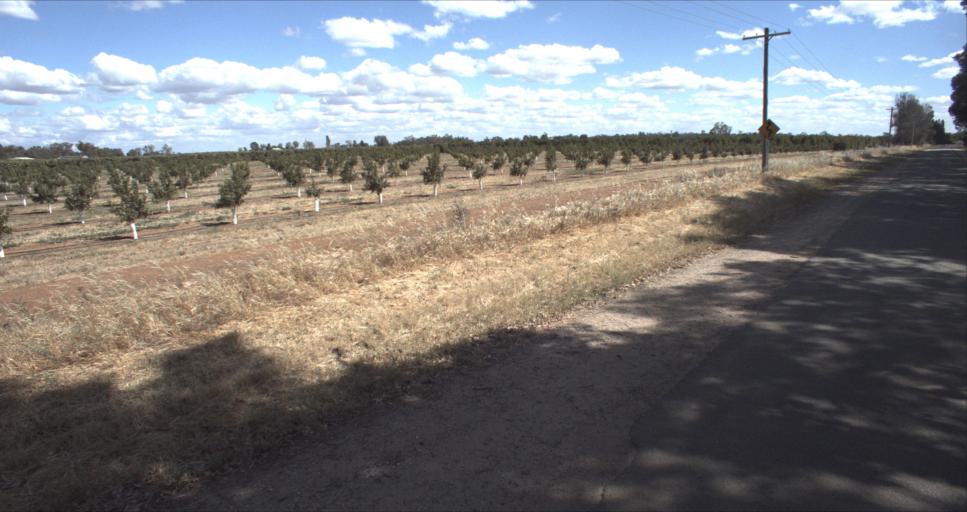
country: AU
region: New South Wales
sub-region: Leeton
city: Leeton
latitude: -34.5094
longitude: 146.2311
